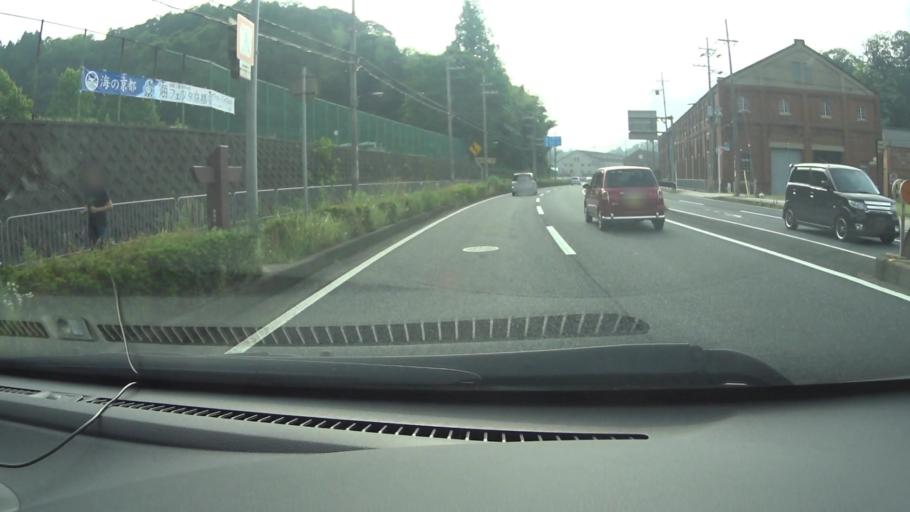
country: JP
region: Kyoto
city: Kameoka
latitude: 35.0211
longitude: 135.5511
